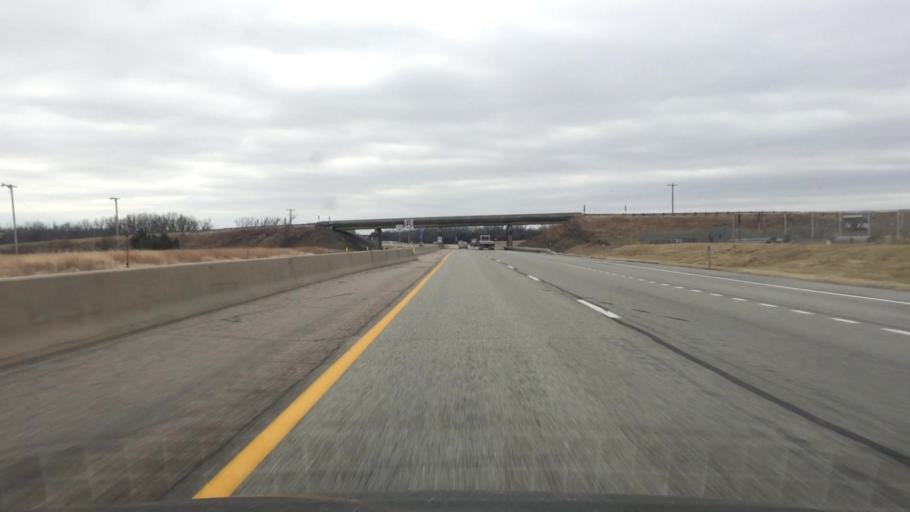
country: US
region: Kansas
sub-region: Butler County
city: El Dorado
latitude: 38.0488
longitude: -96.6379
